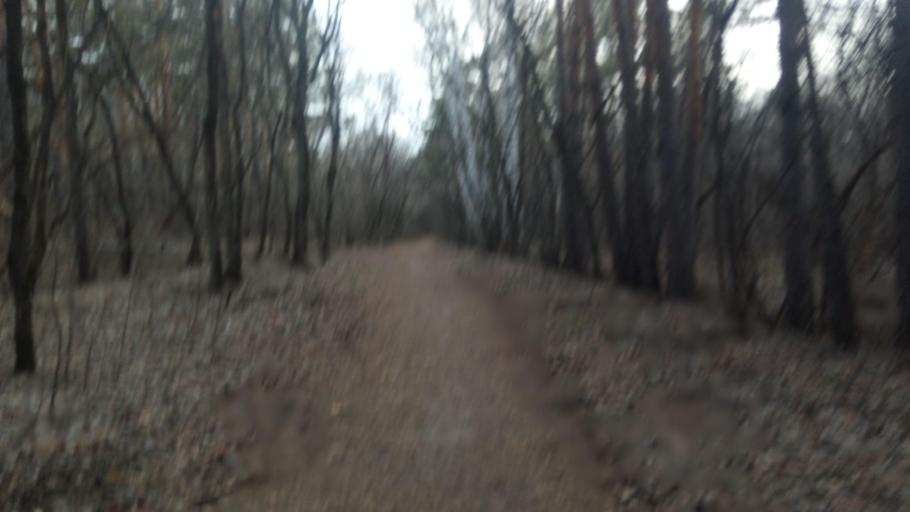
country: RU
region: Chelyabinsk
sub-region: Gorod Chelyabinsk
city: Chelyabinsk
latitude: 55.1457
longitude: 61.3461
